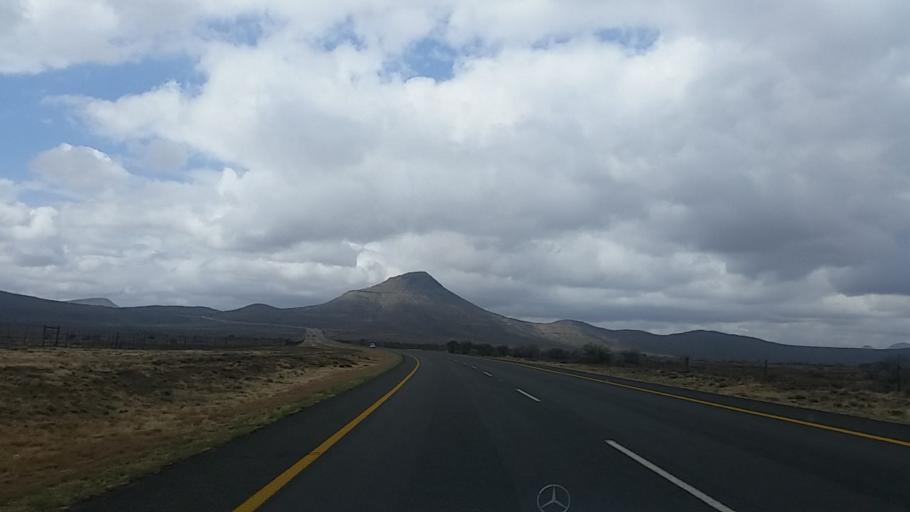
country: ZA
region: Eastern Cape
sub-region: Cacadu District Municipality
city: Graaff-Reinet
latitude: -32.1322
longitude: 24.5845
